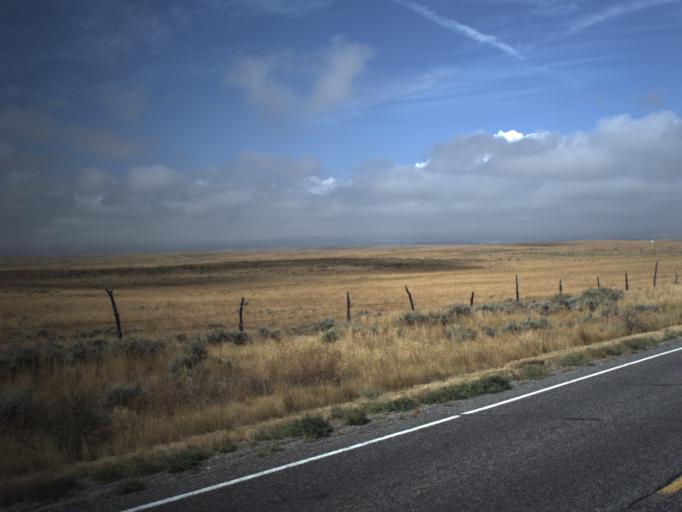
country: US
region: Wyoming
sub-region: Uinta County
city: Evanston
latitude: 41.4511
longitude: -111.0867
